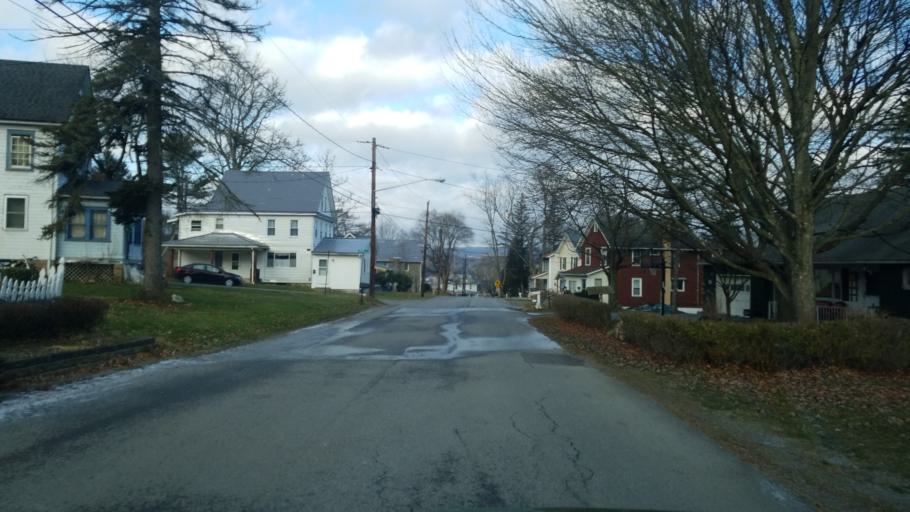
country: US
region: Pennsylvania
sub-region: Clearfield County
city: Clearfield
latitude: 41.0183
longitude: -78.4301
